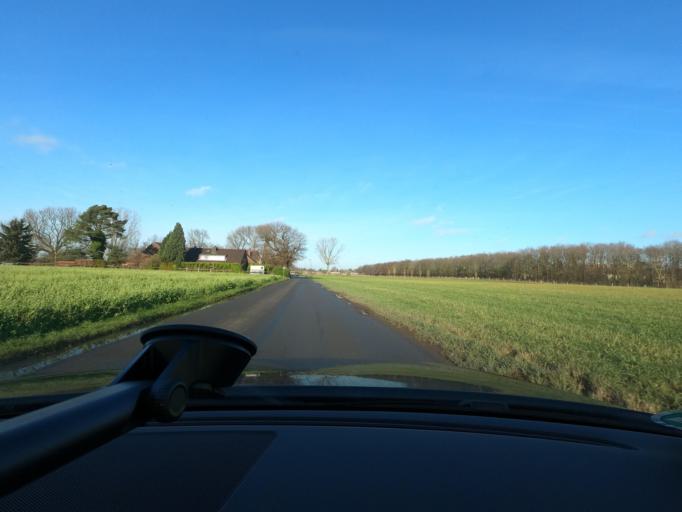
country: DE
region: North Rhine-Westphalia
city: Tonisvorst
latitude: 51.3403
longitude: 6.5208
